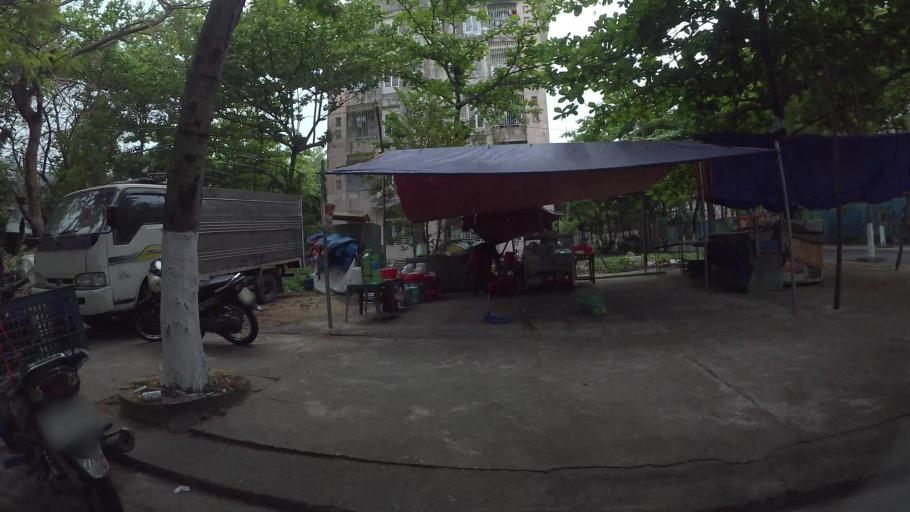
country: VN
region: Da Nang
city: Cam Le
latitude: 16.0301
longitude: 108.2114
